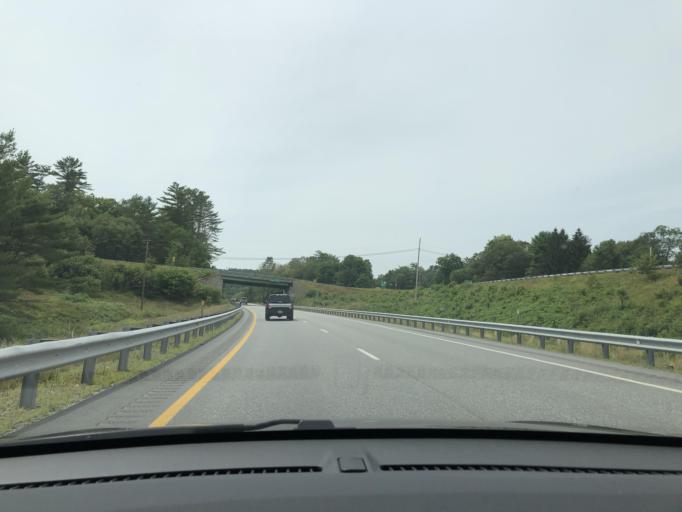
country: US
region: New Hampshire
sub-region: Merrimack County
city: Webster
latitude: 43.2737
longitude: -71.7911
